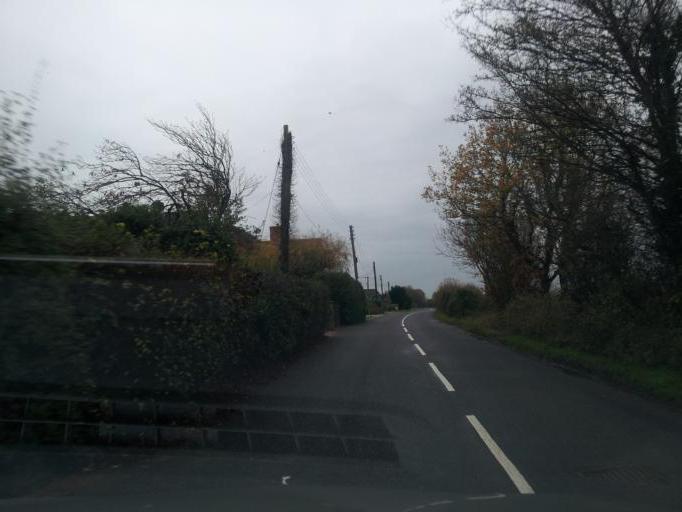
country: GB
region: England
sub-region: Essex
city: Eight Ash Green
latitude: 51.9222
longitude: 0.8017
